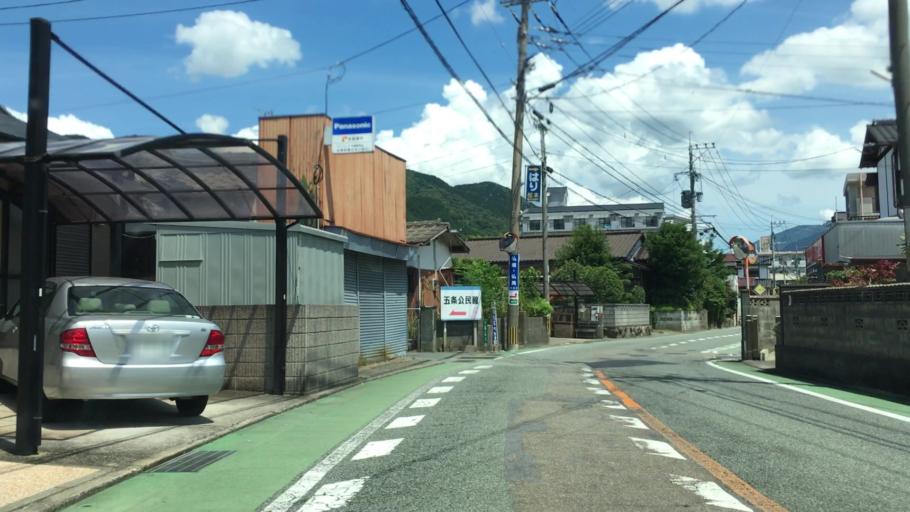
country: JP
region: Fukuoka
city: Dazaifu
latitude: 33.5151
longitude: 130.5267
